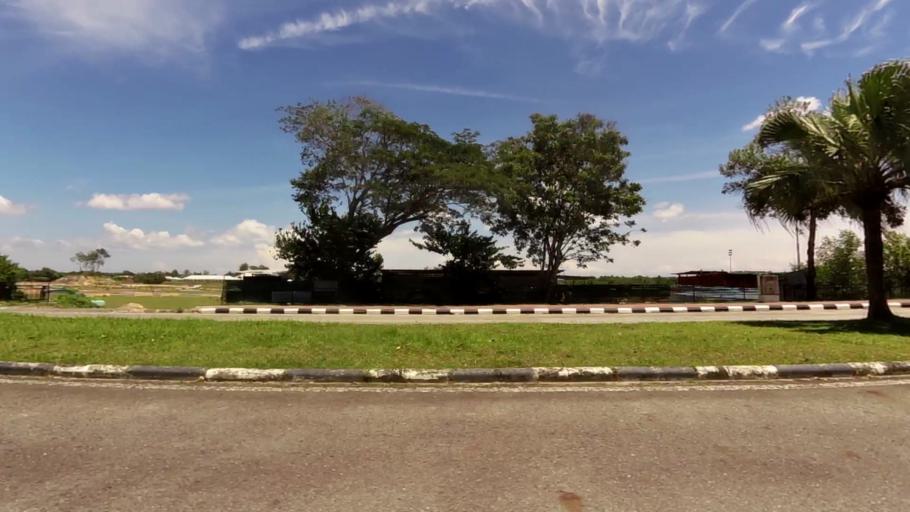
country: BN
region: Brunei and Muara
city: Bandar Seri Begawan
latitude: 4.9244
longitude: 114.9452
